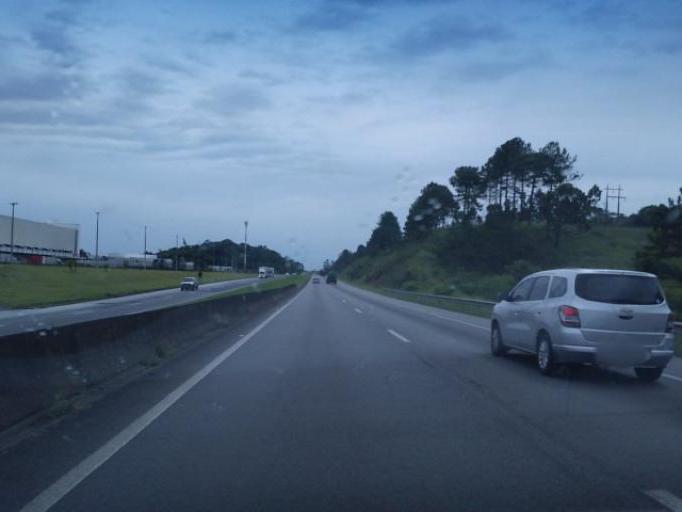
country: BR
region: Sao Paulo
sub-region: Registro
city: Registro
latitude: -24.4434
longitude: -47.8008
